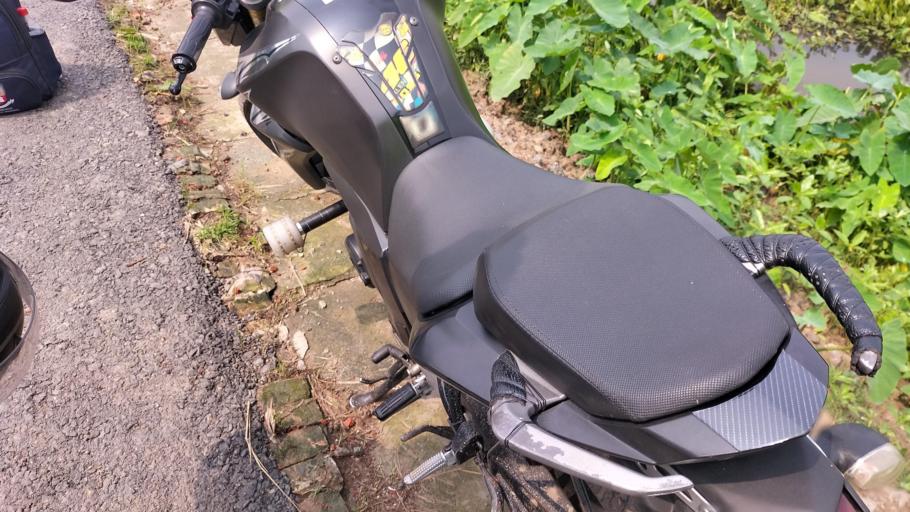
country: BD
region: Dhaka
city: Netrakona
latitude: 24.9222
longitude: 90.8271
